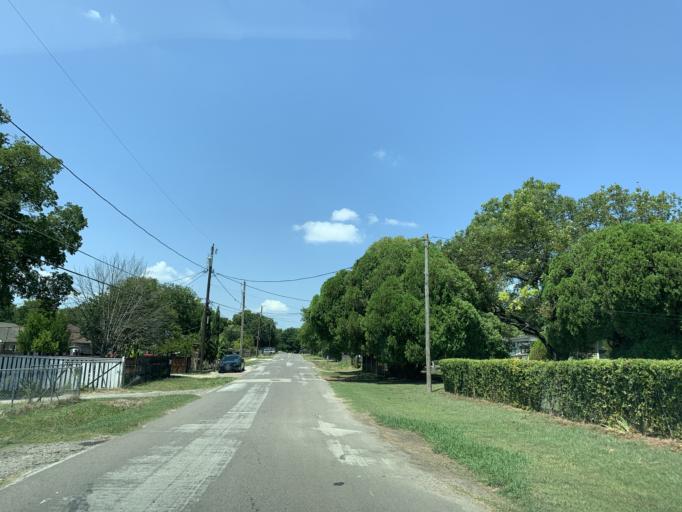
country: US
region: Texas
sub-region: Dallas County
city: Hutchins
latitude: 32.6873
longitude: -96.7762
